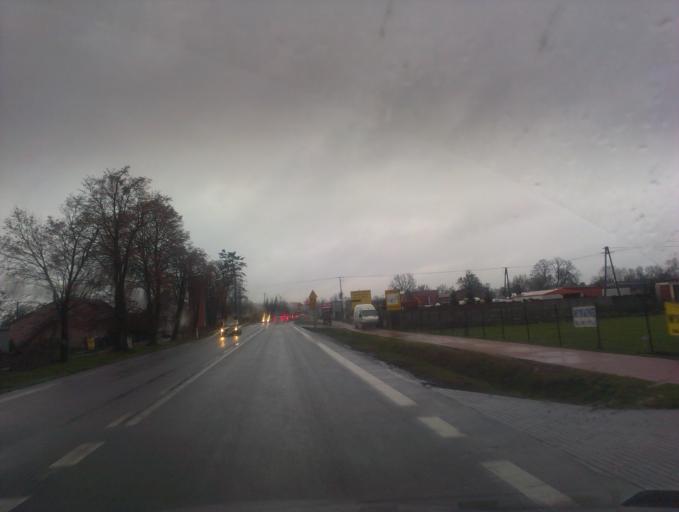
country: PL
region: Greater Poland Voivodeship
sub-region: Powiat obornicki
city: Oborniki
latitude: 52.6247
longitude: 16.8094
